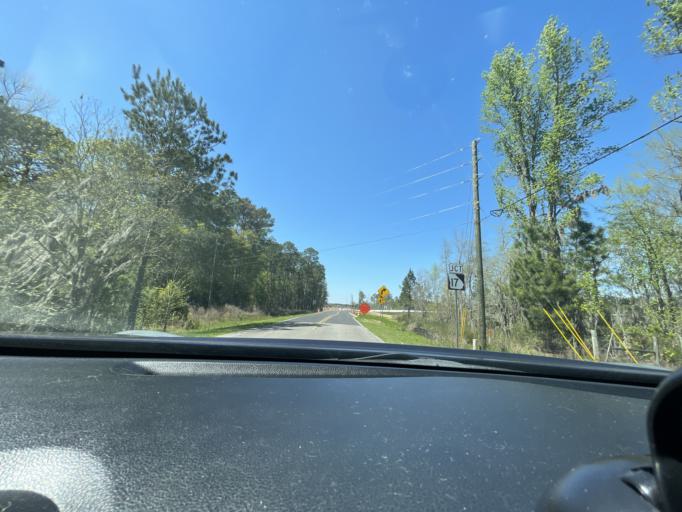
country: US
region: Georgia
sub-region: Chatham County
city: Bloomingdale
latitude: 32.1139
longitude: -81.3145
